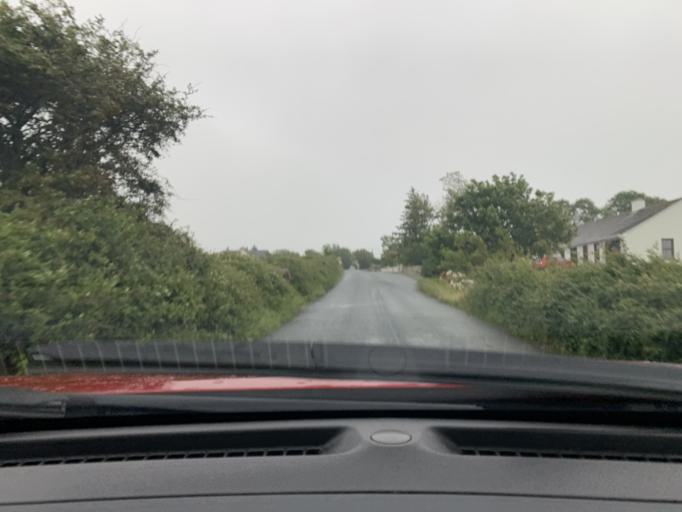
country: IE
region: Connaught
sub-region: County Leitrim
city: Kinlough
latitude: 54.4407
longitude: -8.4377
